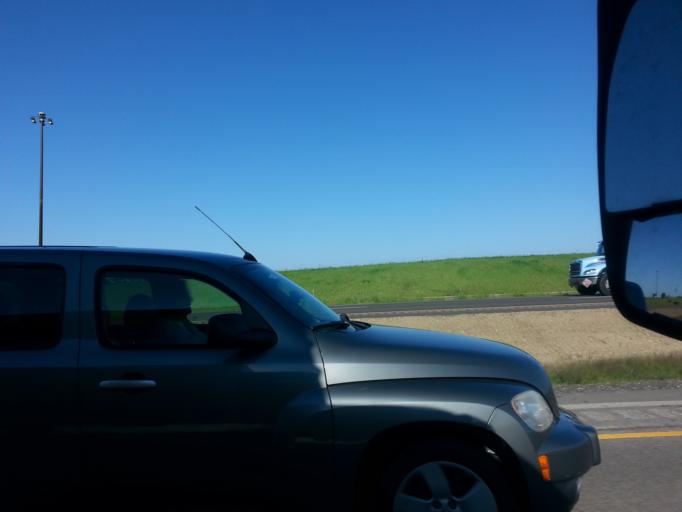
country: US
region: Illinois
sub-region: McLean County
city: Normal
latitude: 40.5581
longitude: -89.0026
